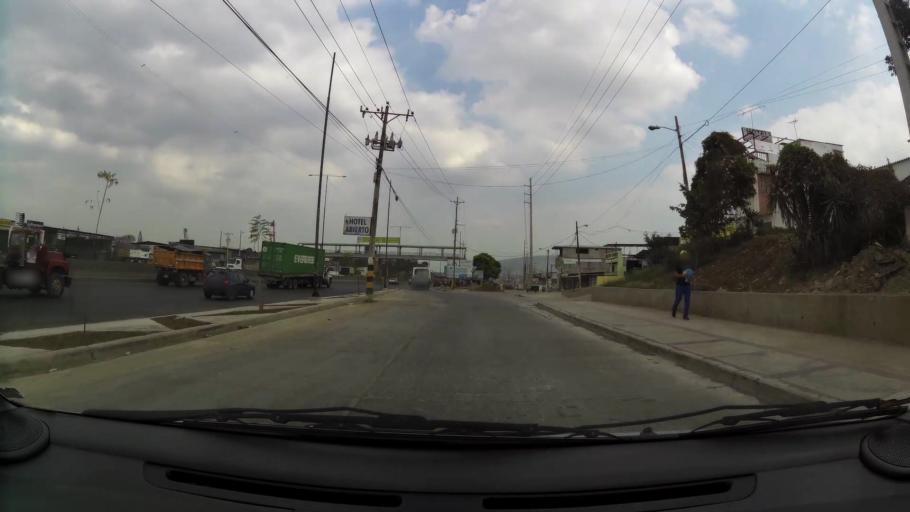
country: EC
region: Guayas
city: Santa Lucia
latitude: -2.1123
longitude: -79.9480
